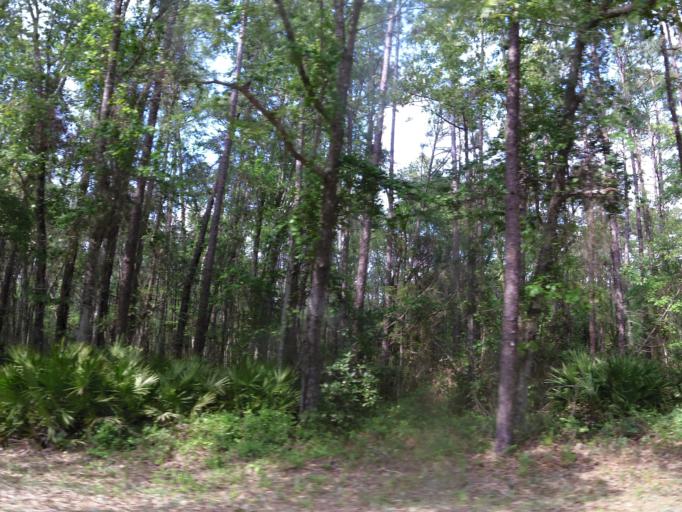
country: US
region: Georgia
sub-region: Charlton County
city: Folkston
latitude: 30.8058
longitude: -82.0388
